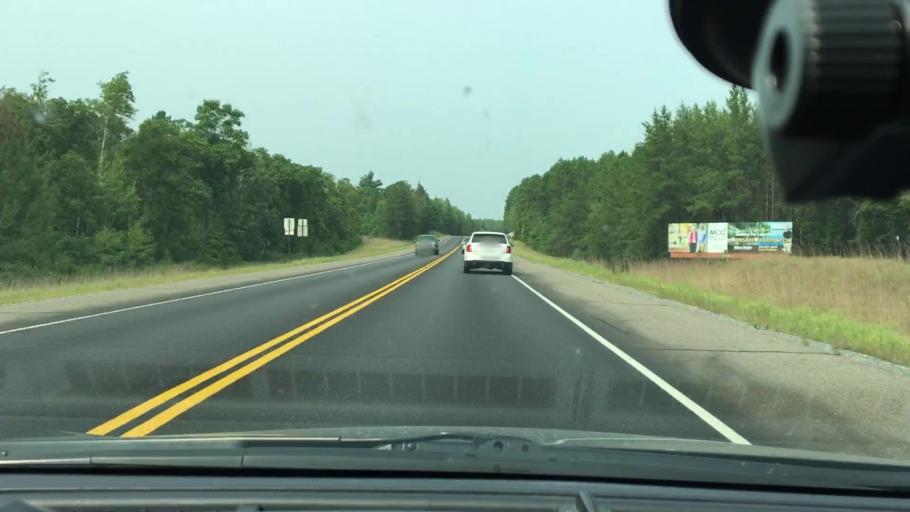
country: US
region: Minnesota
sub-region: Crow Wing County
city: Cross Lake
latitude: 46.6192
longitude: -94.1319
